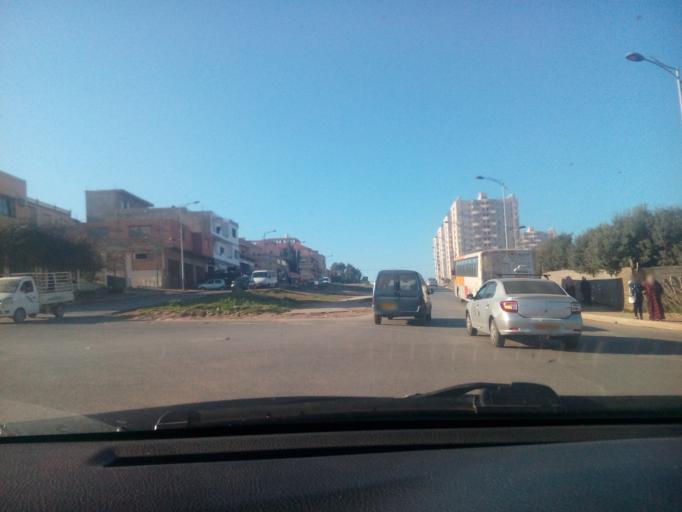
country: DZ
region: Oran
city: Bir el Djir
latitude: 35.7506
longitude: -0.5524
